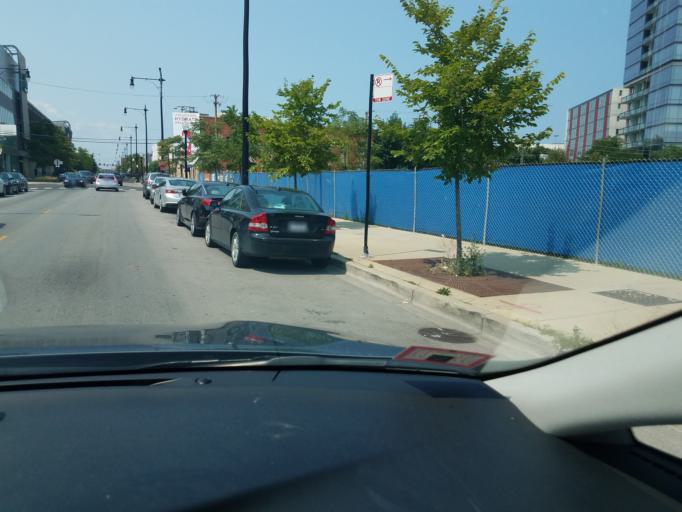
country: US
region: Illinois
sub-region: Cook County
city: Chicago
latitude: 41.9077
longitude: -87.6514
